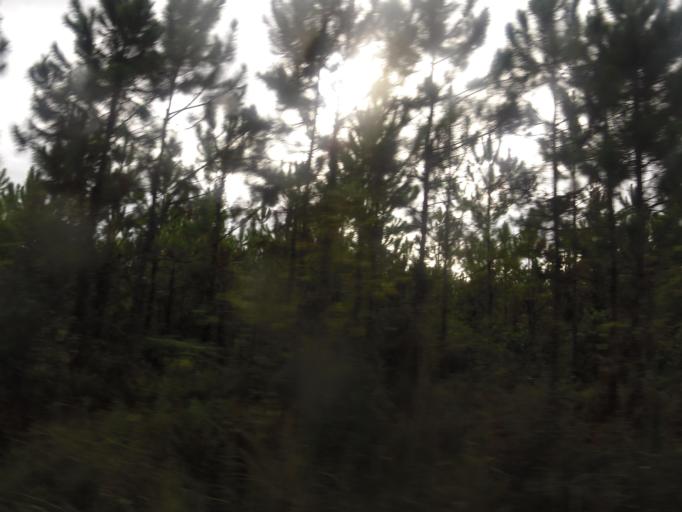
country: US
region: Florida
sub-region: Flagler County
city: Bunnell
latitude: 29.5501
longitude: -81.3274
